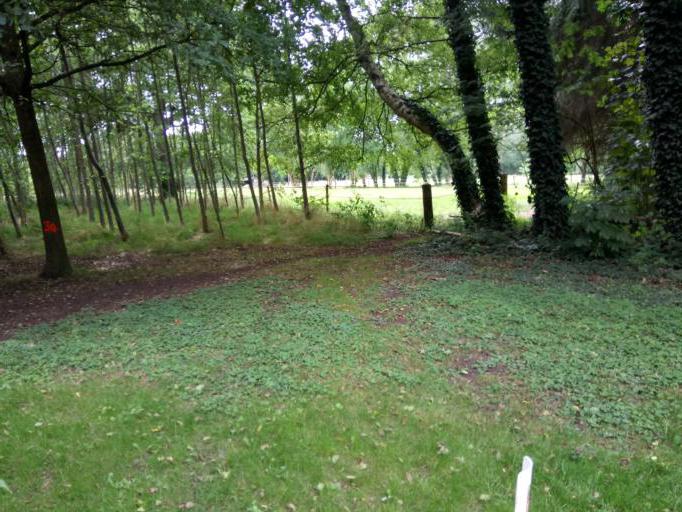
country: BE
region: Flanders
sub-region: Provincie Antwerpen
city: Mol
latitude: 51.2153
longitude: 5.1218
